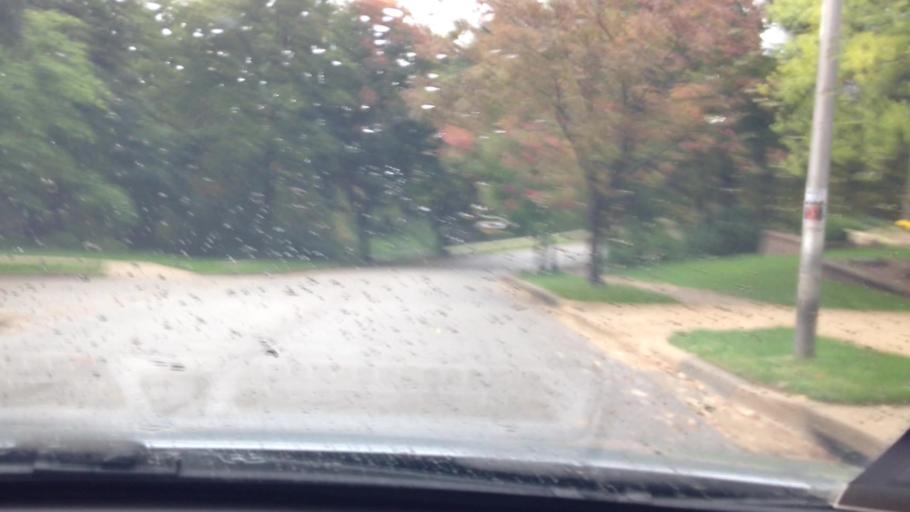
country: US
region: Missouri
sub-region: Platte County
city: Riverside
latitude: 39.1770
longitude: -94.5978
